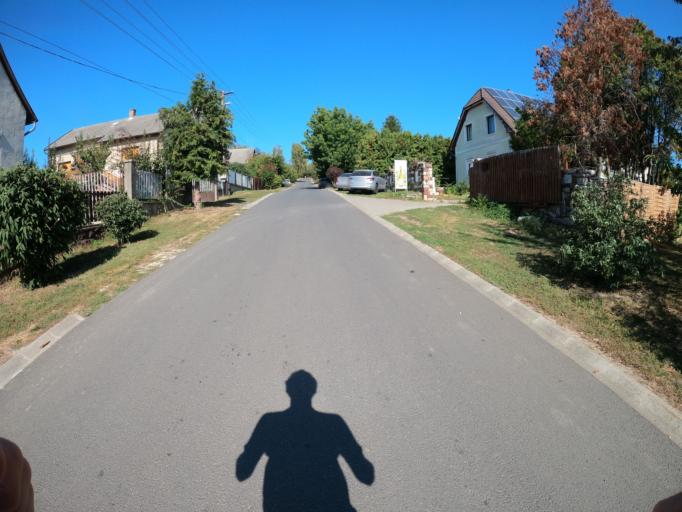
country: HU
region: Veszprem
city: Revfueloep
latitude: 46.8885
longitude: 17.5673
